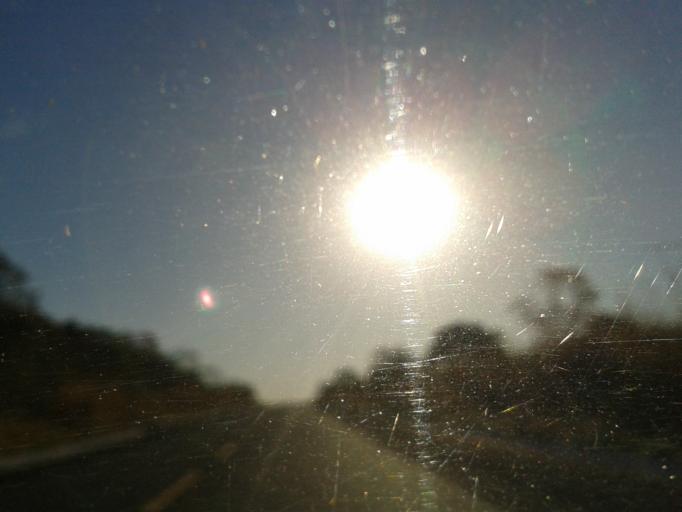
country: BR
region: Minas Gerais
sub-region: Santa Vitoria
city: Santa Vitoria
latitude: -19.1245
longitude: -50.2796
